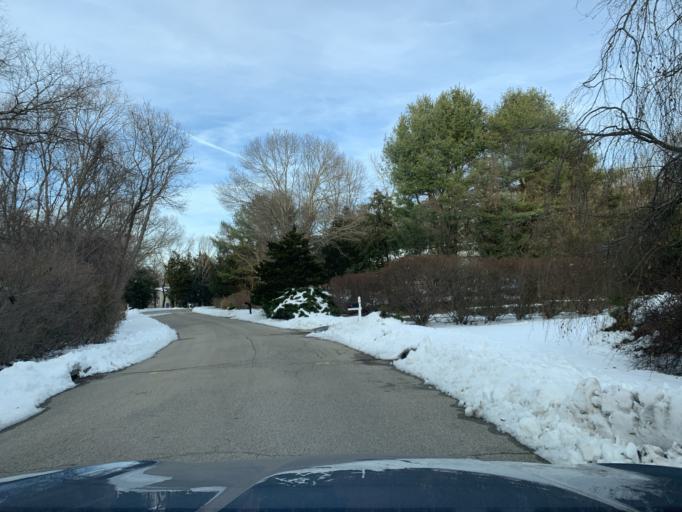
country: US
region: Rhode Island
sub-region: Washington County
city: North Kingstown
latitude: 41.5869
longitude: -71.4369
